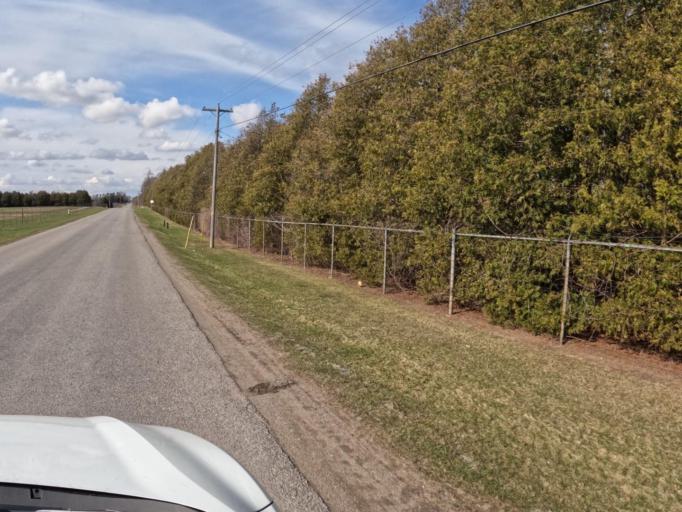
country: CA
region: Ontario
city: Norfolk County
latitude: 42.8534
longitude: -80.2713
